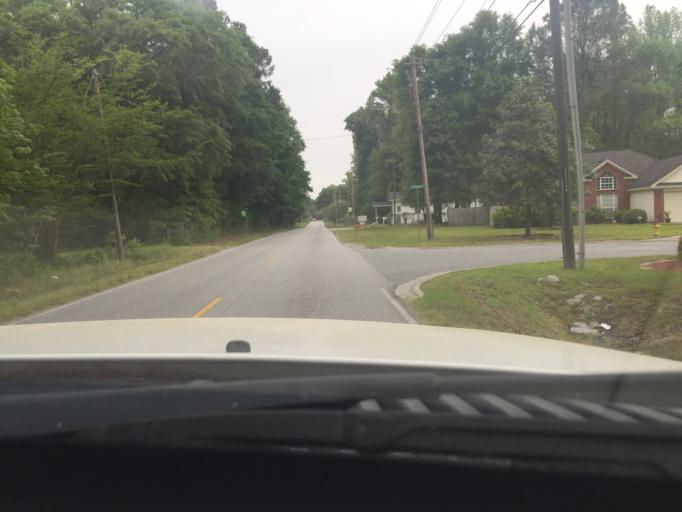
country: US
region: Georgia
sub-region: Chatham County
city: Georgetown
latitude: 31.9726
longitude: -81.2459
